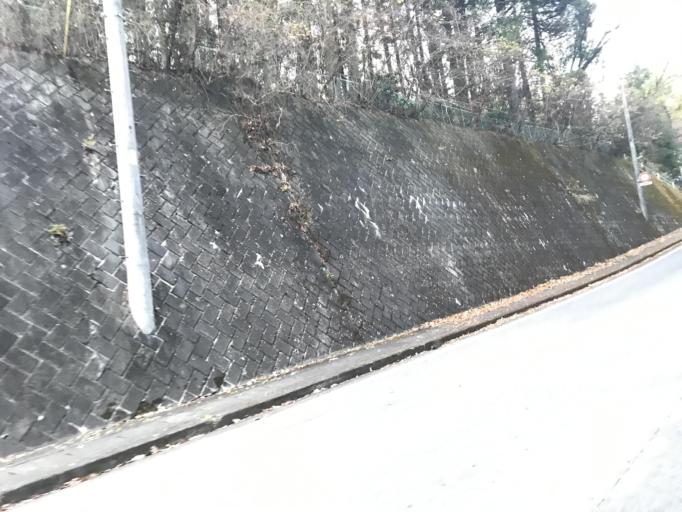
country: JP
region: Tochigi
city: Imaichi
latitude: 36.6744
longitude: 139.7124
